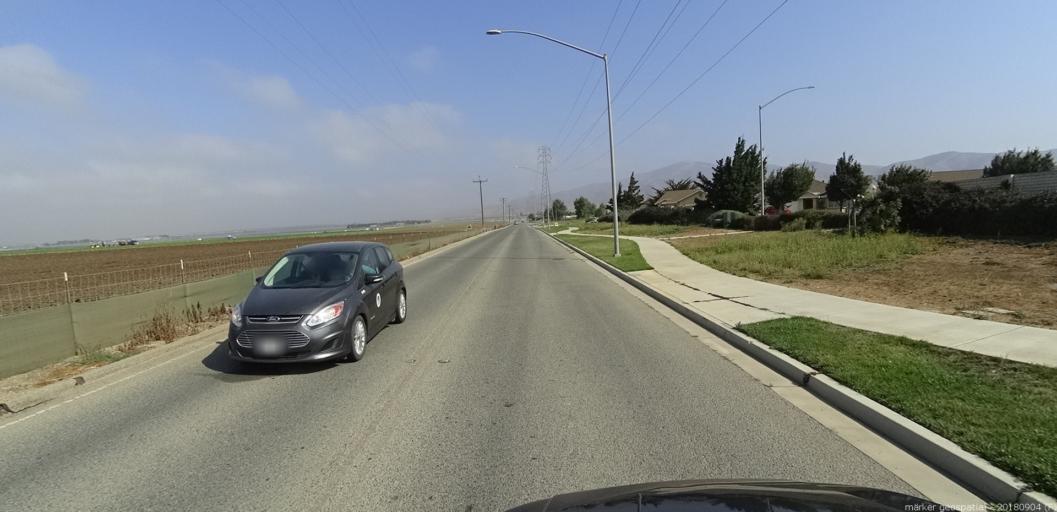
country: US
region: California
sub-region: Monterey County
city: Soledad
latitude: 36.4338
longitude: -121.3336
